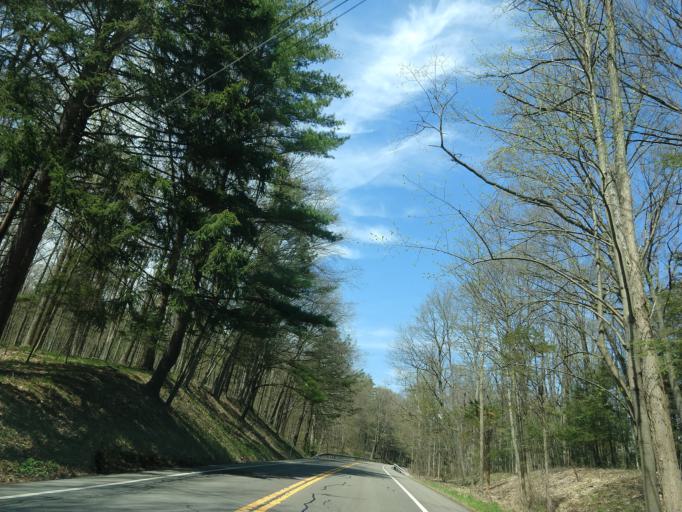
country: US
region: New York
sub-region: Tompkins County
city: Trumansburg
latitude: 42.5397
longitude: -76.5918
